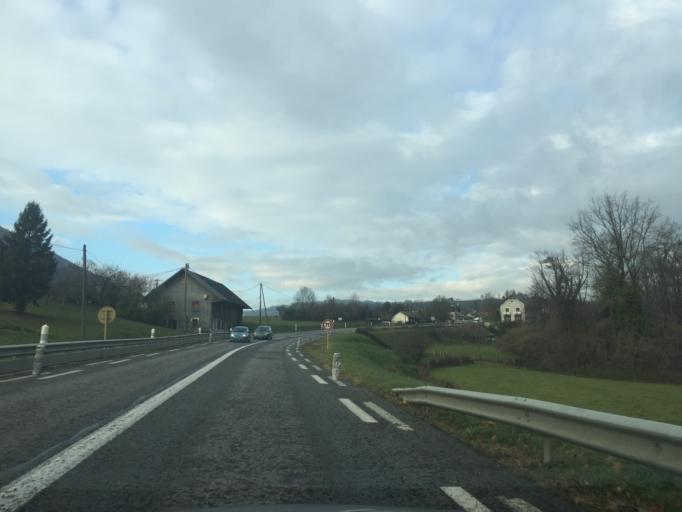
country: FR
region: Rhone-Alpes
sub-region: Departement de la Savoie
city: La Biolle
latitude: 45.7424
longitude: 5.9224
